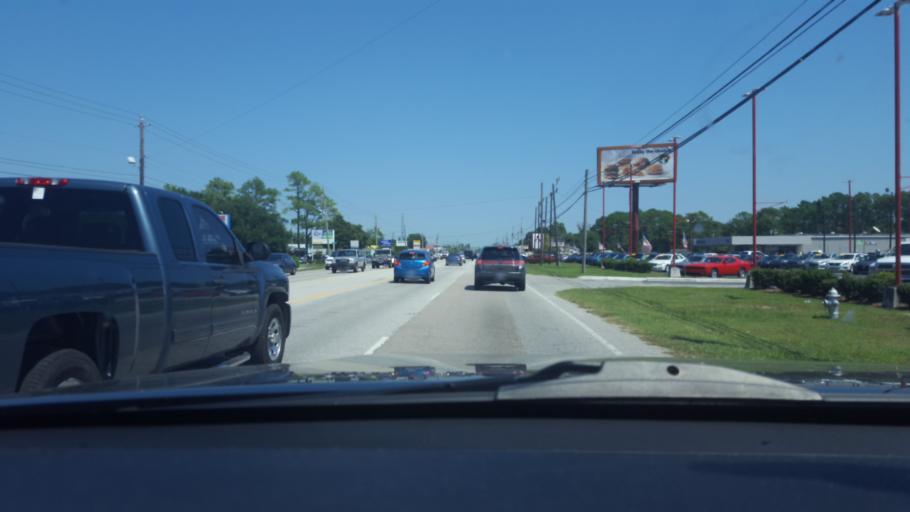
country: US
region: North Carolina
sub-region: New Hanover County
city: Kings Grant
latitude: 34.2529
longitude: -77.8505
